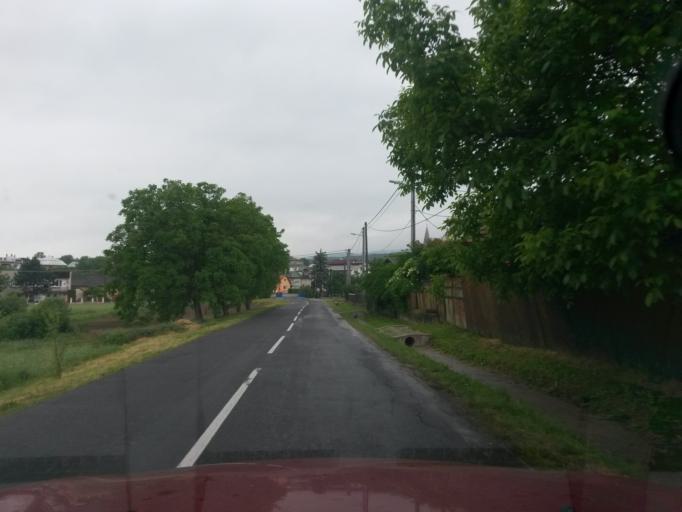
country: SK
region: Kosicky
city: Moldava nad Bodvou
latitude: 48.6860
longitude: 21.0736
